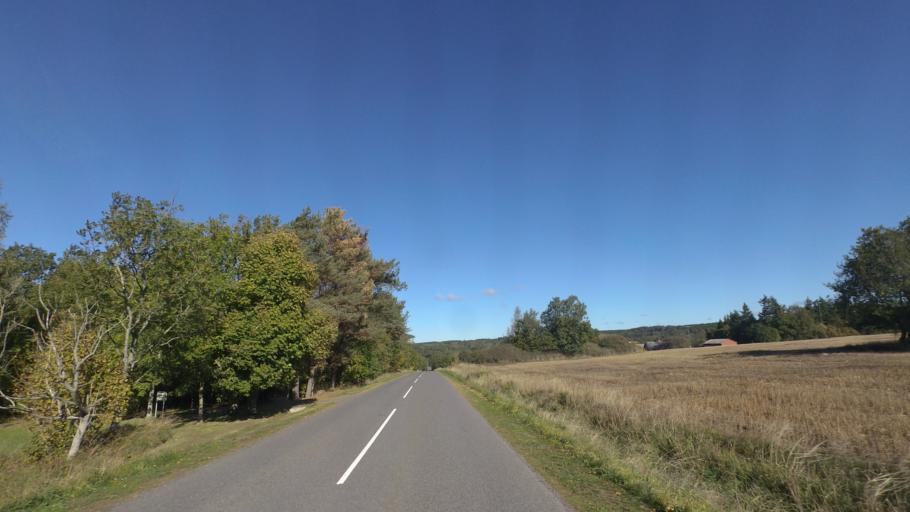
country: DK
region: Capital Region
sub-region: Bornholm Kommune
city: Nexo
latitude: 55.0719
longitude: 15.0818
